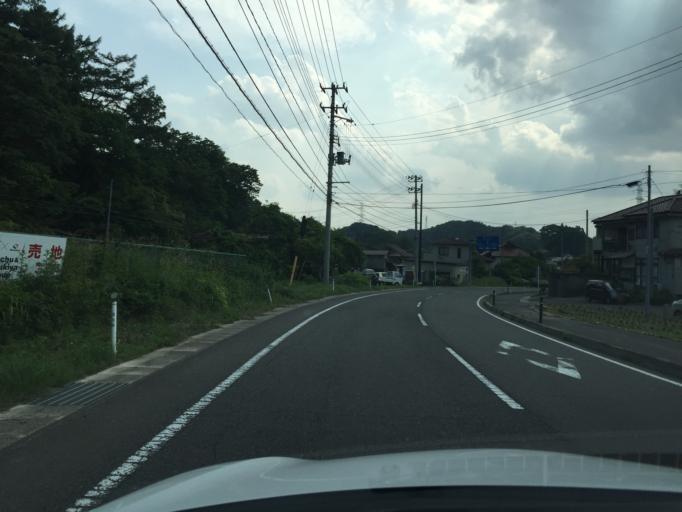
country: JP
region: Fukushima
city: Miharu
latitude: 37.3963
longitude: 140.4552
